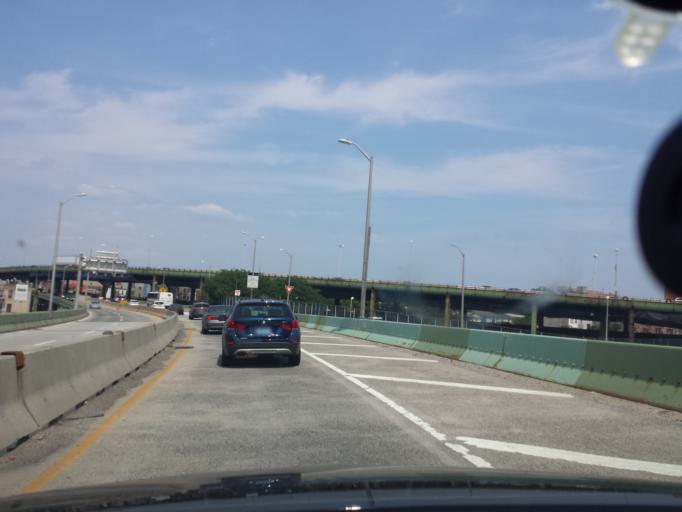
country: US
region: New York
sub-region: Kings County
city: Bensonhurst
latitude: 40.6402
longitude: -74.0233
